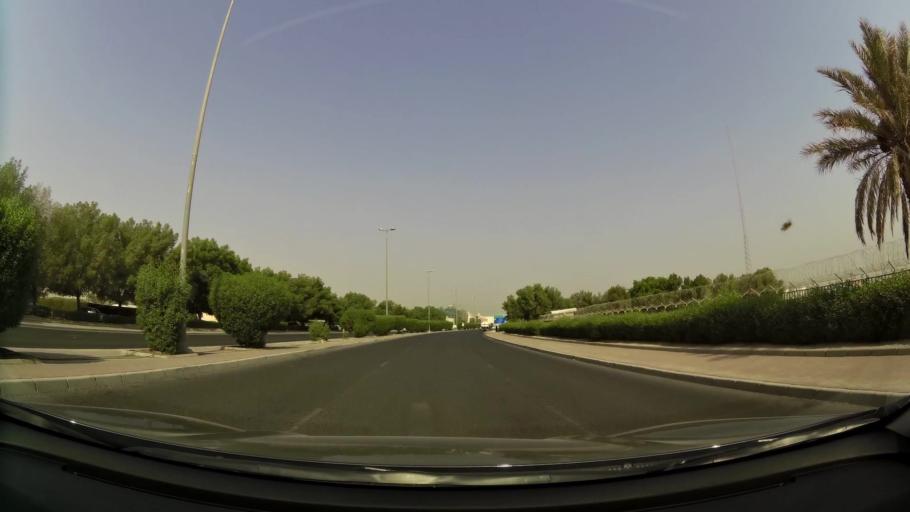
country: KW
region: Al Asimah
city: Ar Rabiyah
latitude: 29.2889
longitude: 47.8801
